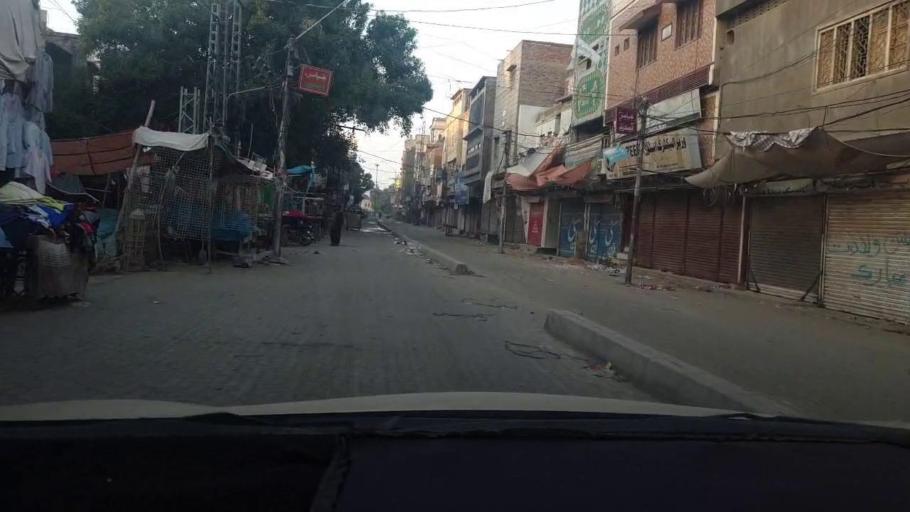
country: PK
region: Sindh
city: Larkana
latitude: 27.5544
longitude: 68.2156
